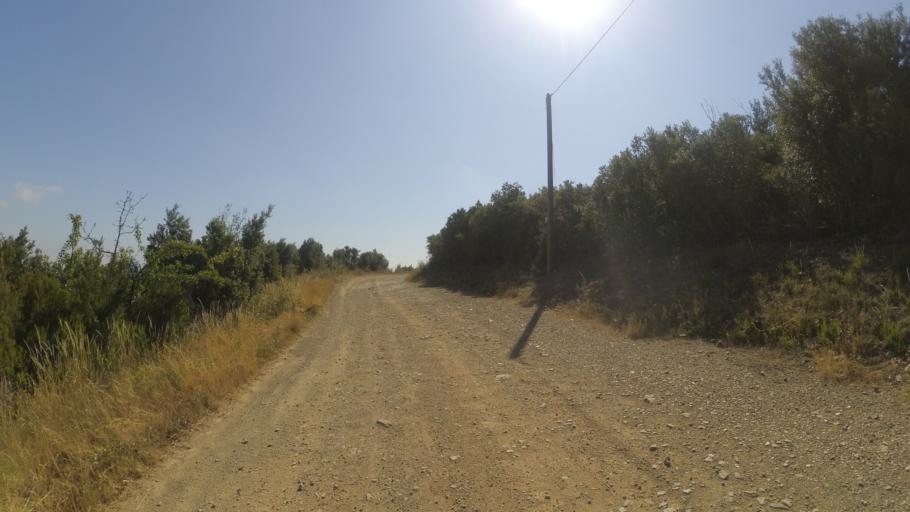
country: FR
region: Languedoc-Roussillon
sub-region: Departement des Pyrenees-Orientales
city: Thuir
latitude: 42.6156
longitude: 2.6795
